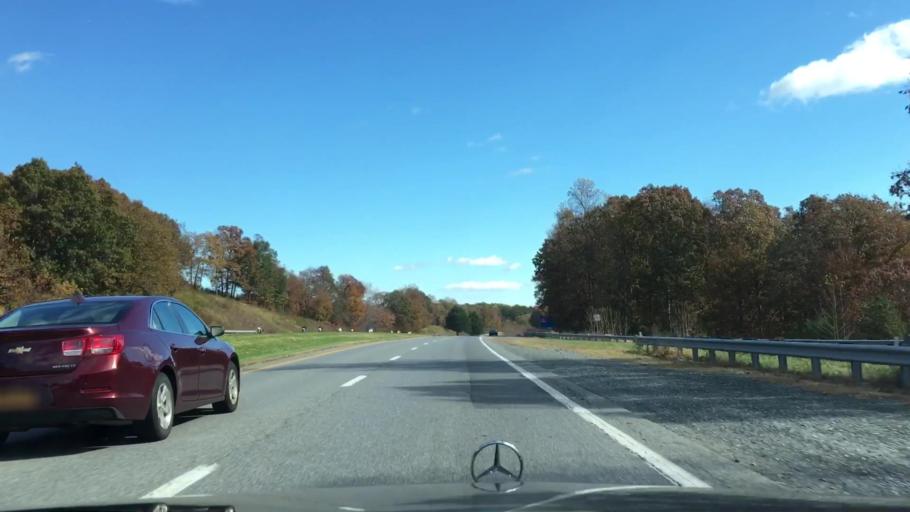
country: US
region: Virginia
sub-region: Campbell County
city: Altavista
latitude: 37.1388
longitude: -79.2674
